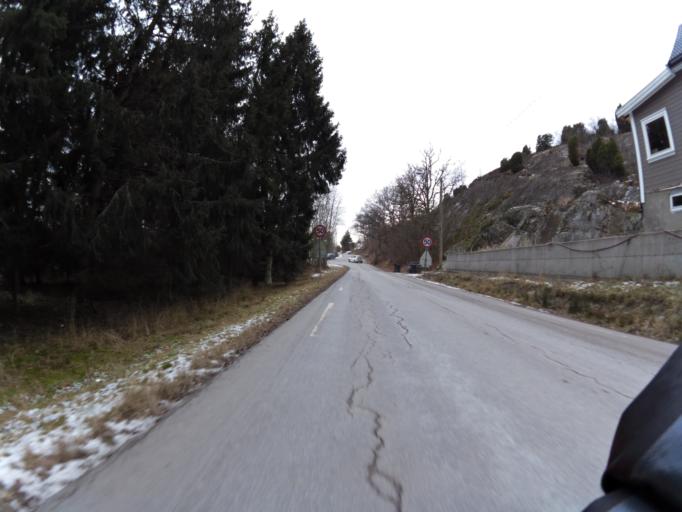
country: NO
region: Ostfold
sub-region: Fredrikstad
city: Fredrikstad
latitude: 59.2118
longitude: 10.8887
